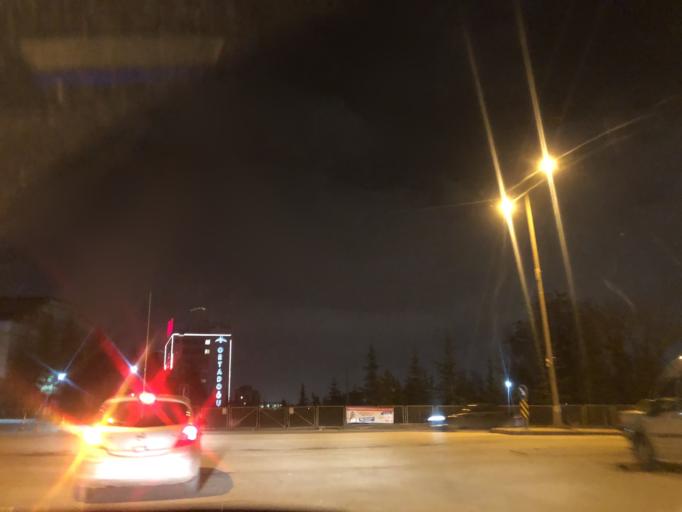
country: TR
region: Ankara
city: Batikent
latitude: 39.9643
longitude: 32.7974
